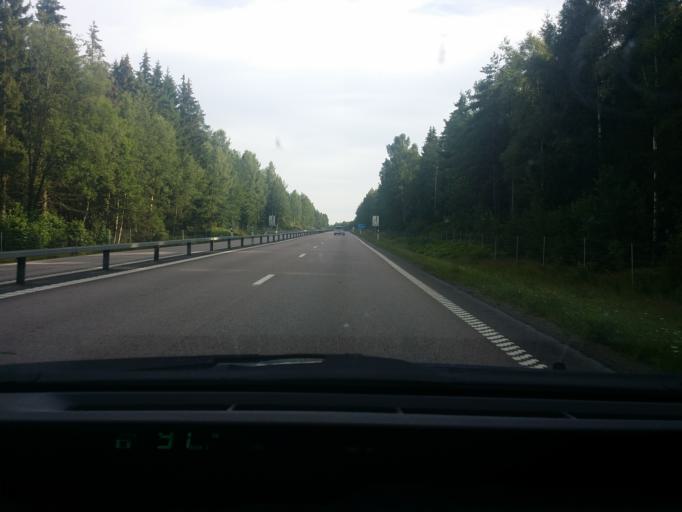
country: SE
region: Vaestmanland
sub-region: Vasteras
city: Hokasen
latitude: 59.6609
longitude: 16.5793
